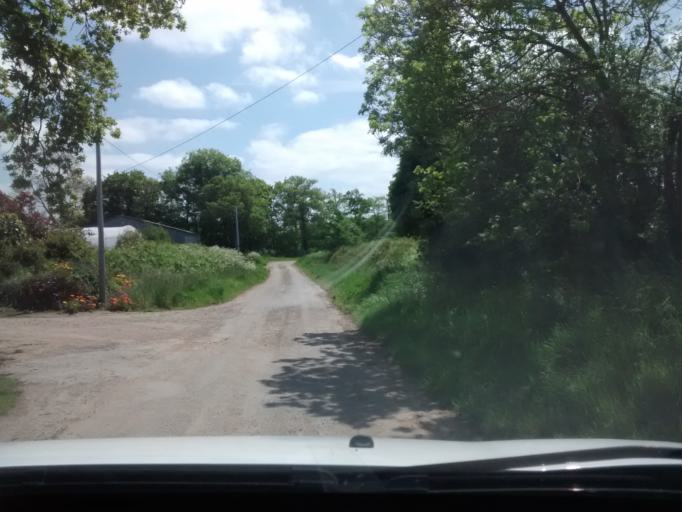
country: FR
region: Brittany
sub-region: Departement des Cotes-d'Armor
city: Louannec
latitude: 48.7877
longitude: -3.4115
